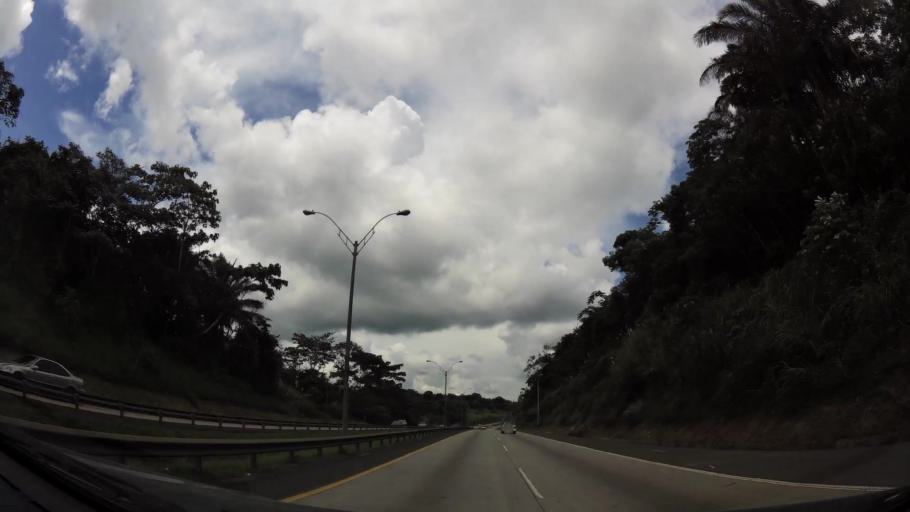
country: PA
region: Panama
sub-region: Distrito Arraijan
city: Arraijan
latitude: 8.9787
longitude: -79.6461
